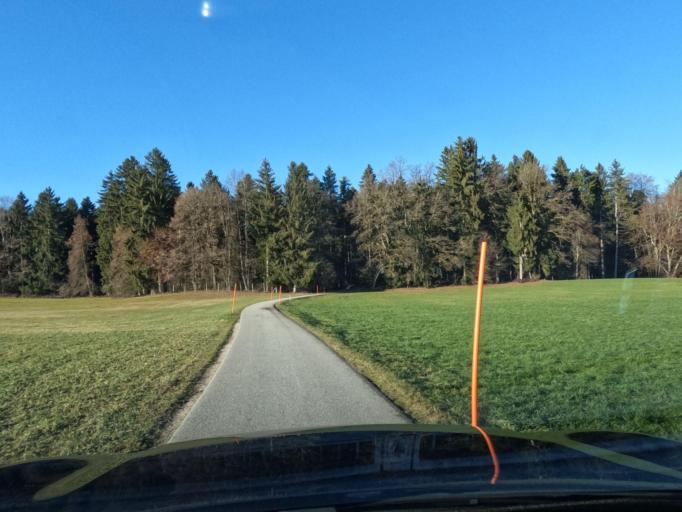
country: DE
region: Bavaria
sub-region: Upper Bavaria
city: Surberg
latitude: 47.8827
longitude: 12.6861
